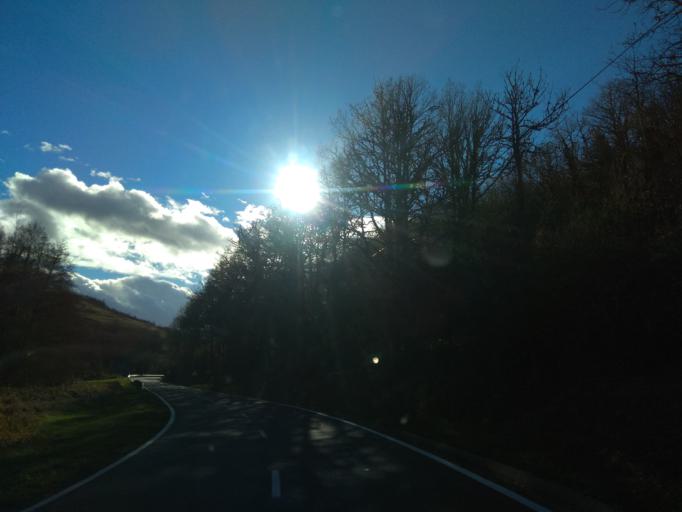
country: ES
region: Cantabria
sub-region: Provincia de Cantabria
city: San Martin de Elines
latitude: 42.8927
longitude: -3.9064
